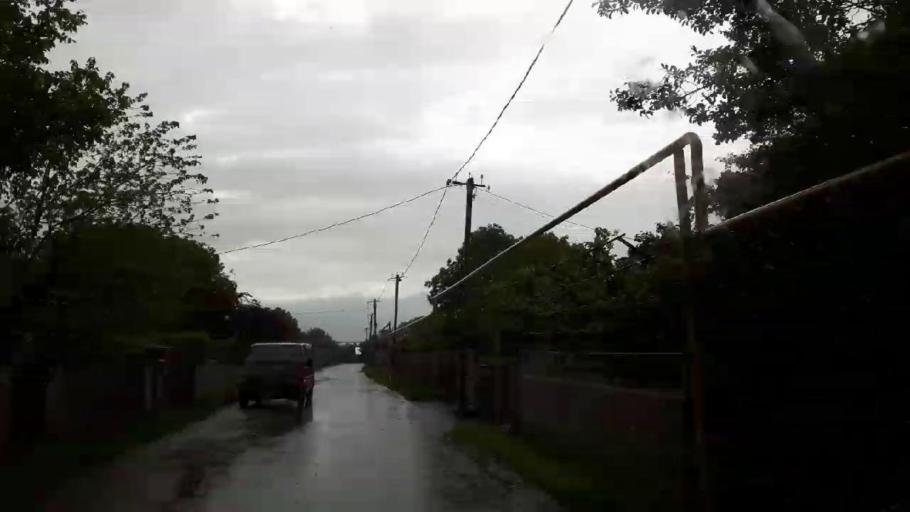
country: GE
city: Agara
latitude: 42.0125
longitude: 43.7739
